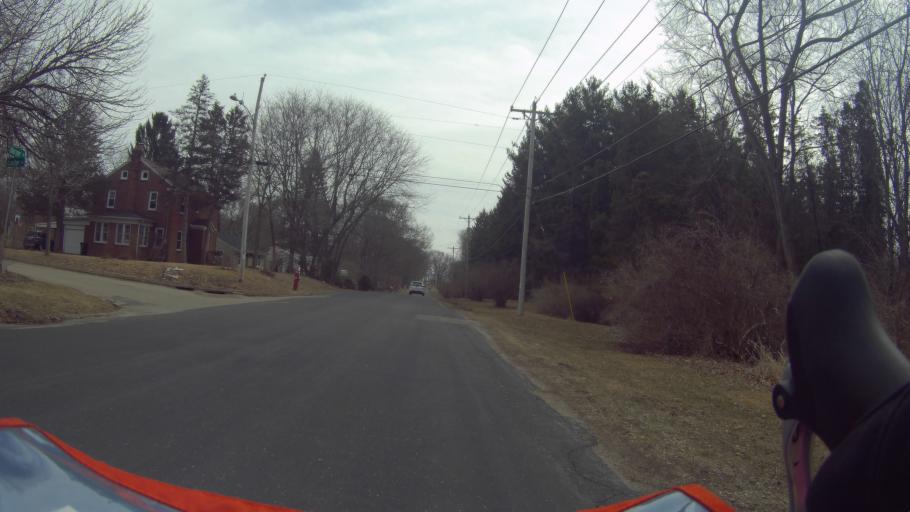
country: US
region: Wisconsin
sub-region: Dane County
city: Maple Bluff
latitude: 43.1325
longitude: -89.3932
